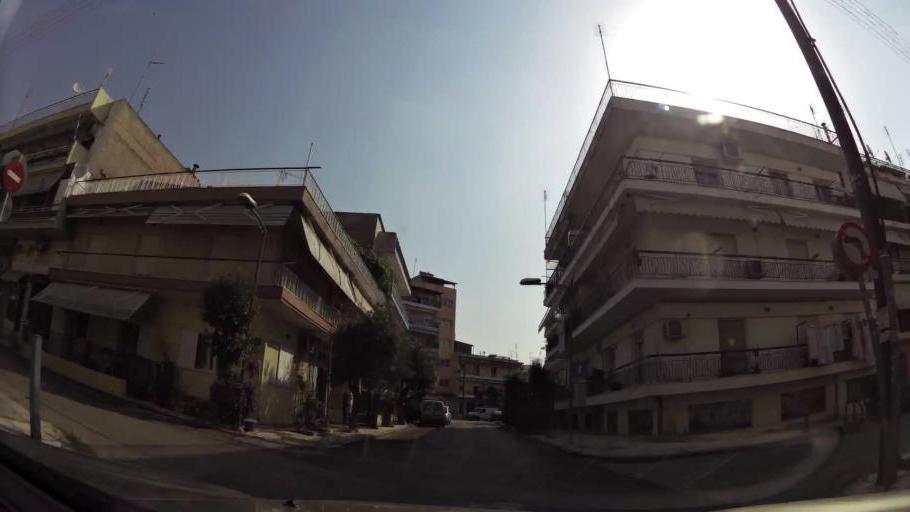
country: GR
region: Central Macedonia
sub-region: Nomos Thessalonikis
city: Stavroupoli
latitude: 40.6729
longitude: 22.9303
